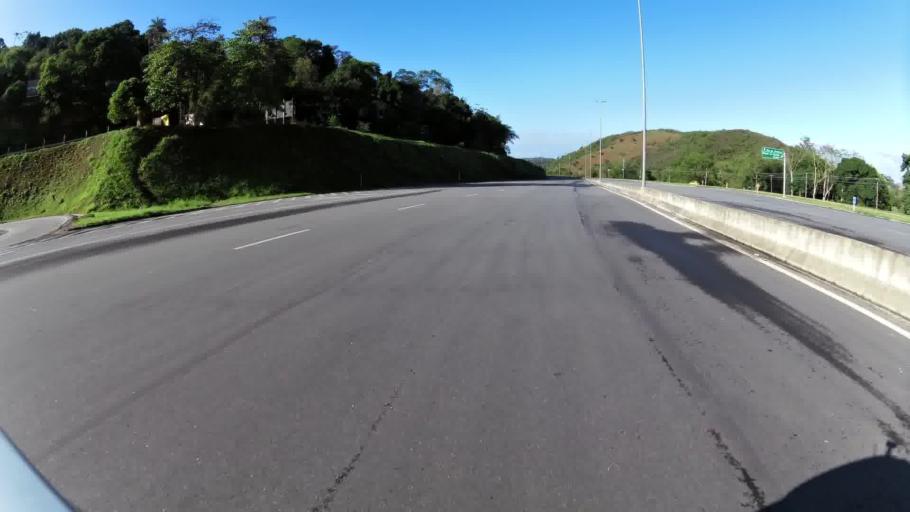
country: BR
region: Rio de Janeiro
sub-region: Petropolis
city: Petropolis
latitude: -22.6114
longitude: -43.2858
